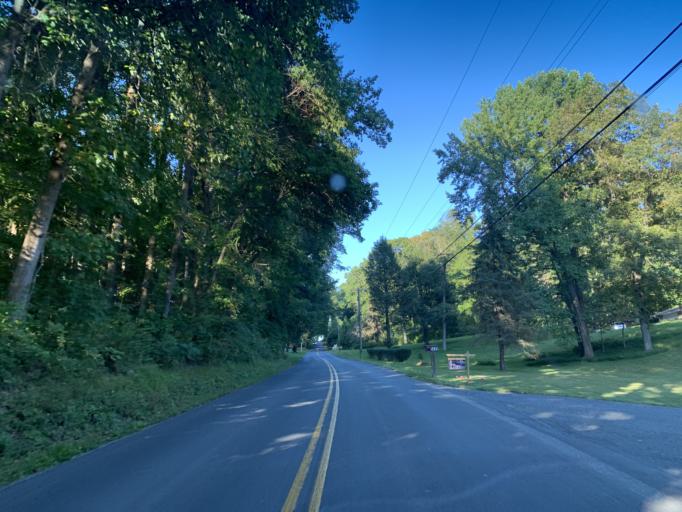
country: US
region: Maryland
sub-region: Harford County
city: Jarrettsville
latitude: 39.5885
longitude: -76.4481
